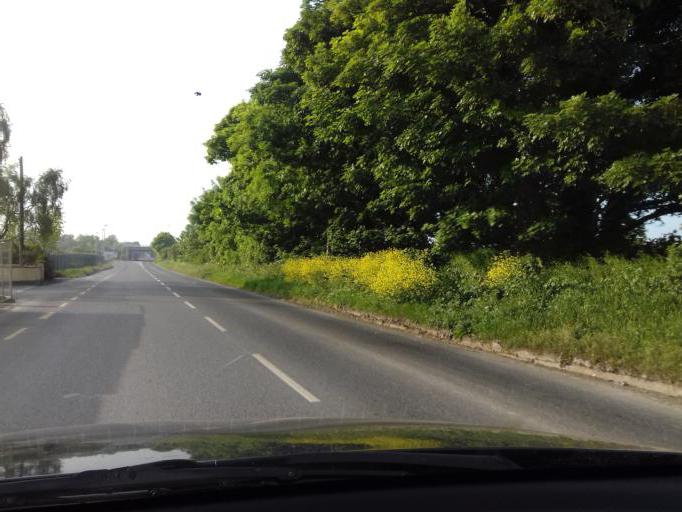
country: IE
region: Leinster
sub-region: Dublin City
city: Finglas
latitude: 53.4165
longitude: -6.3214
